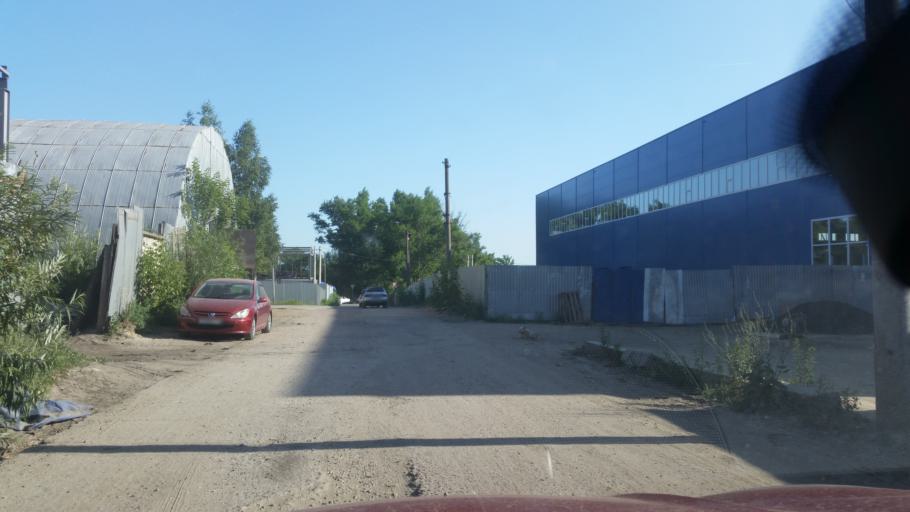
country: RU
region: Orjol
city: Znamenka
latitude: 52.9195
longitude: 35.9866
